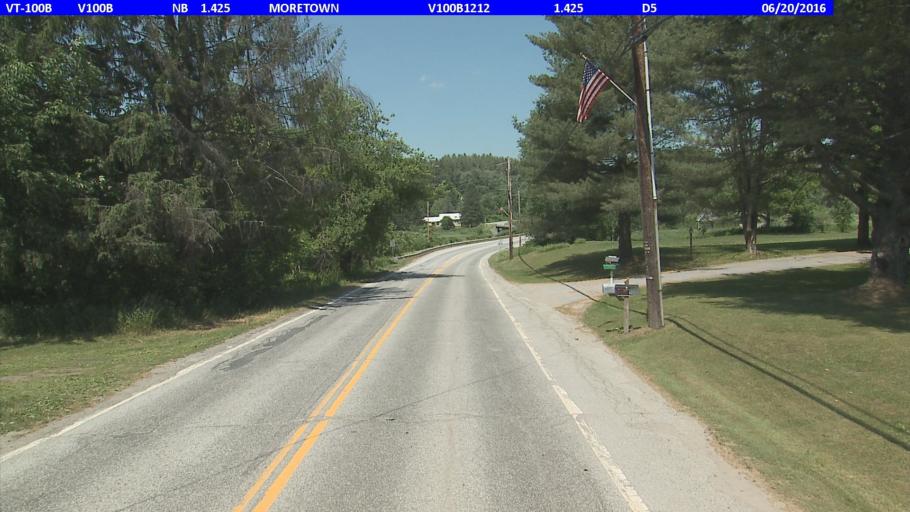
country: US
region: Vermont
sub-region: Washington County
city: Waterbury
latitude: 44.2539
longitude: -72.7585
